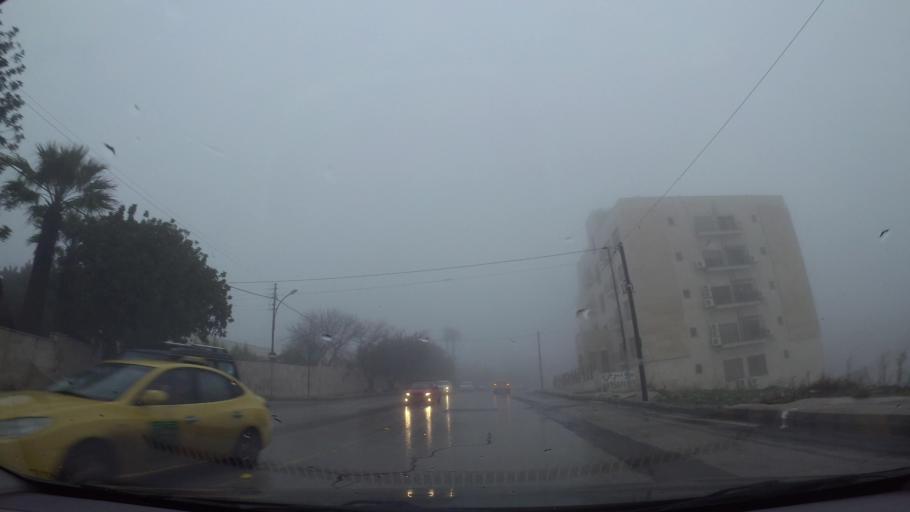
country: JO
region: Amman
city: Al Jubayhah
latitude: 32.0108
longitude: 35.8823
